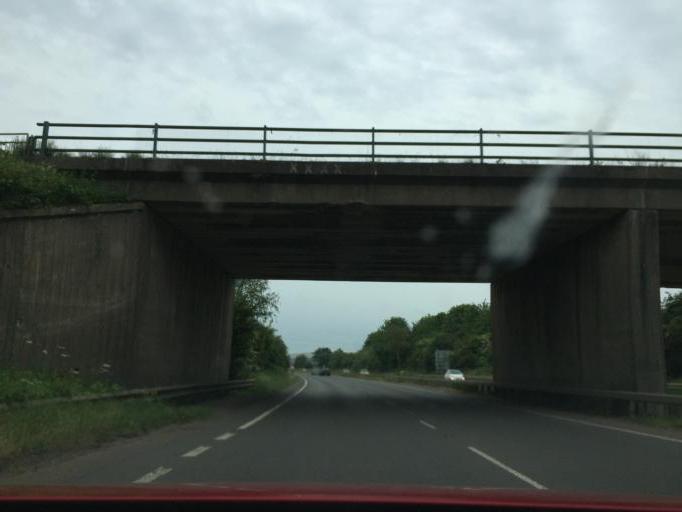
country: GB
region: England
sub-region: Warwickshire
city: Nuneaton
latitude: 52.5076
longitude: -1.4761
